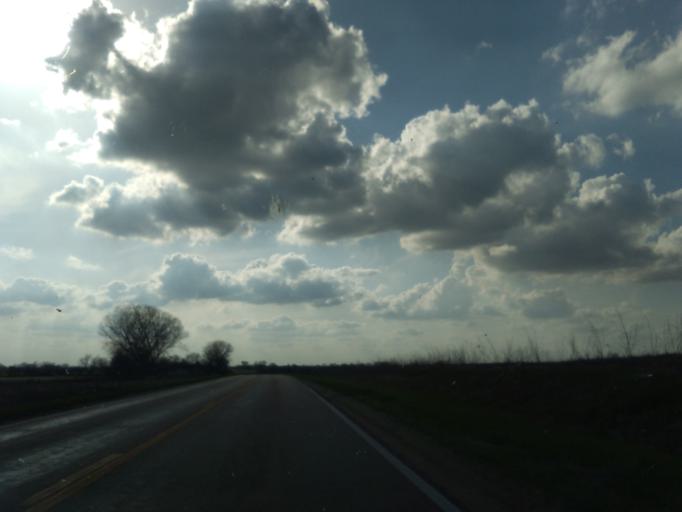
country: US
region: Nebraska
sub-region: Webster County
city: Red Cloud
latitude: 40.0918
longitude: -98.6207
